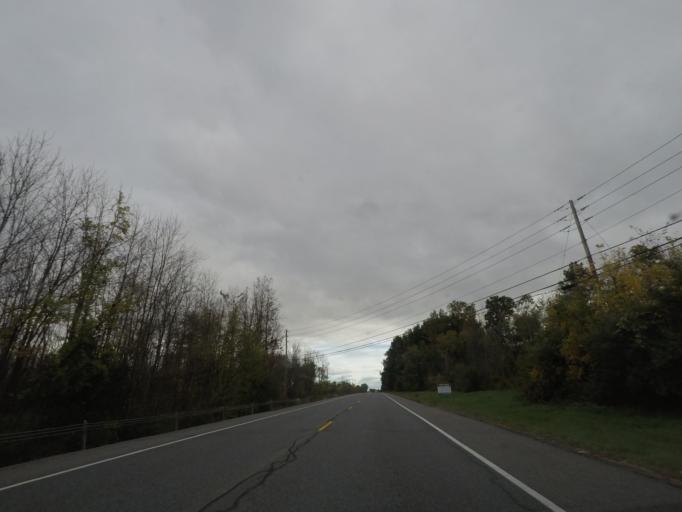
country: US
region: New York
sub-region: Saratoga County
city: Mechanicville
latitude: 42.8741
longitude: -73.7246
